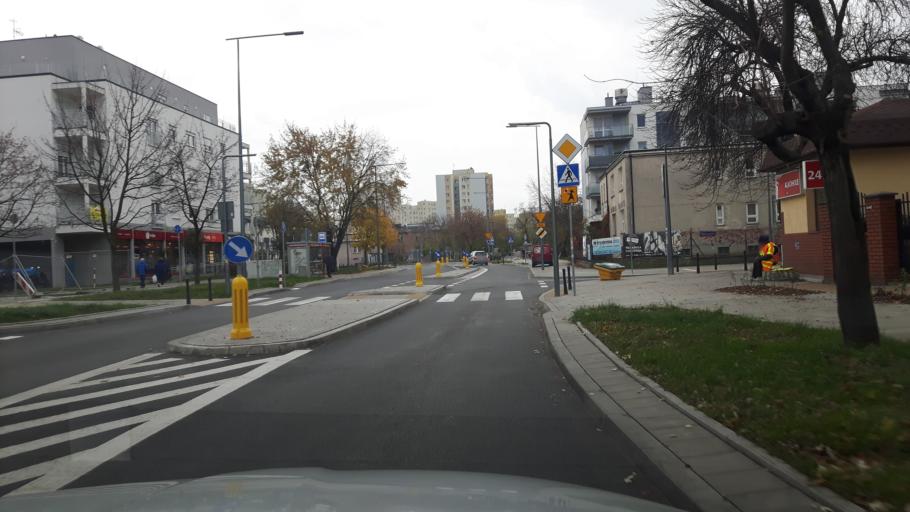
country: PL
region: Masovian Voivodeship
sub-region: Warszawa
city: Targowek
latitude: 52.2711
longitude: 21.0575
